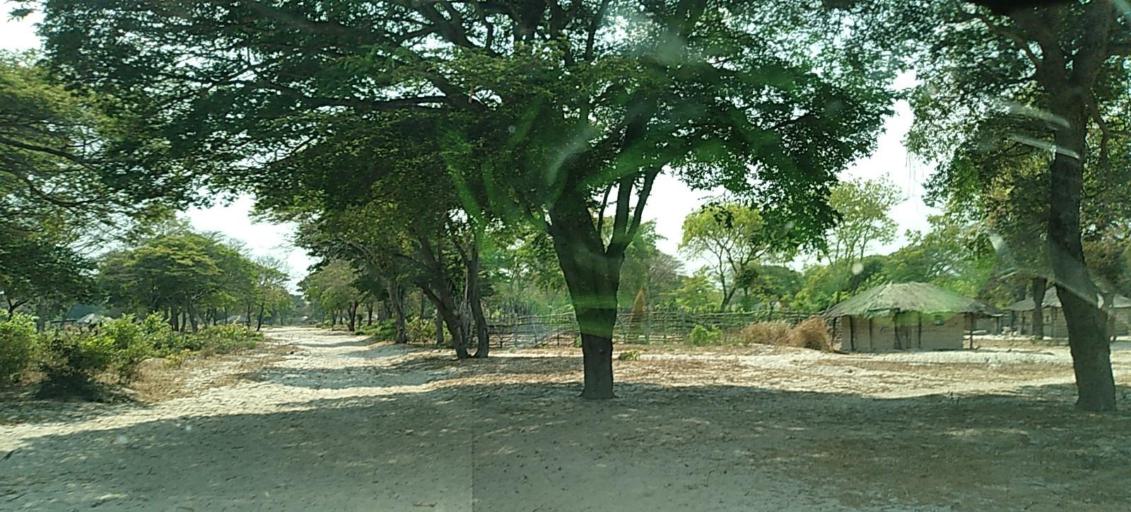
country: ZM
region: North-Western
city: Kabompo
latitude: -13.3862
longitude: 23.7702
